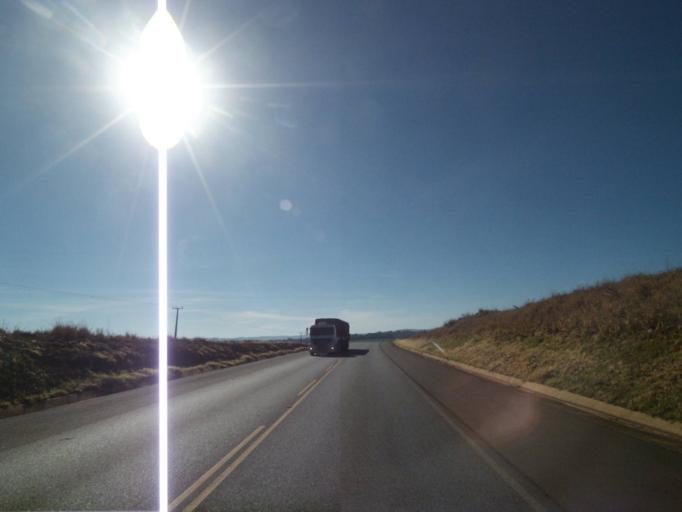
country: BR
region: Parana
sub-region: Tibagi
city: Tibagi
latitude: -24.4322
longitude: -50.4125
